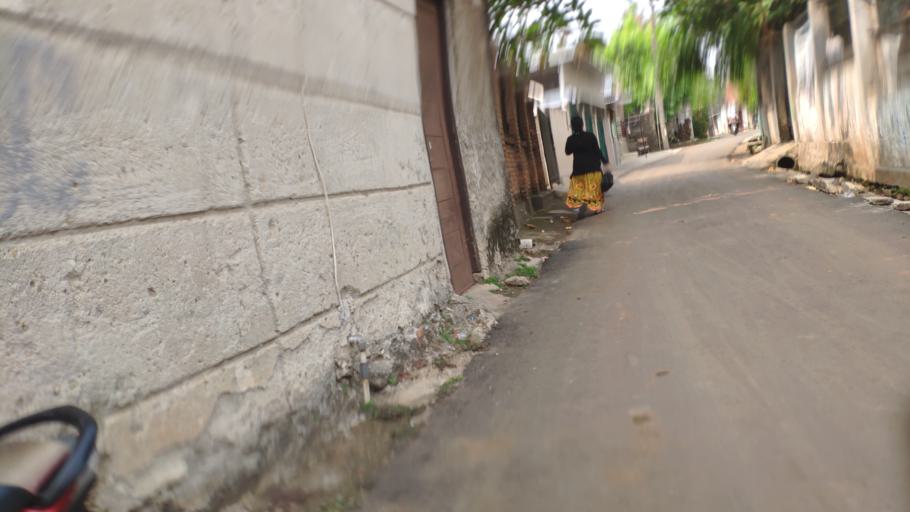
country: ID
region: West Java
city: Depok
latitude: -6.3469
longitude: 106.8075
